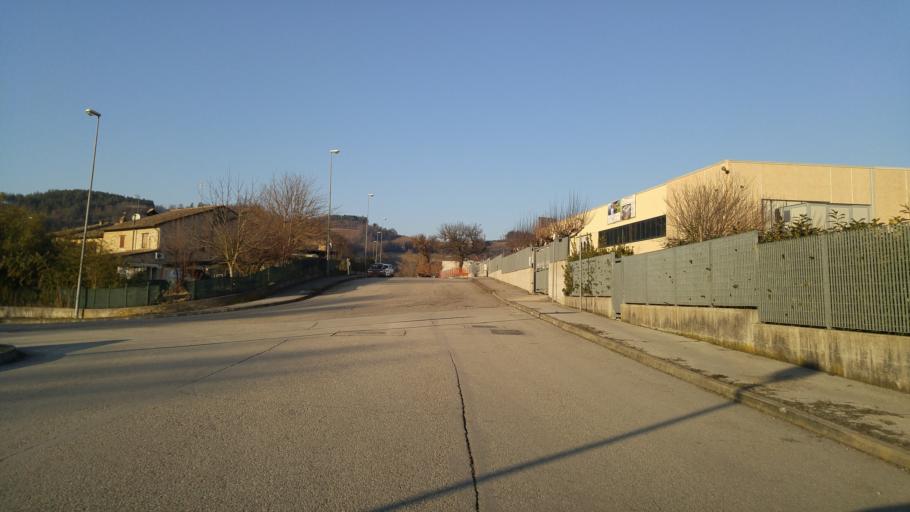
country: IT
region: The Marches
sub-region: Provincia di Pesaro e Urbino
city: Fermignano
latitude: 43.6876
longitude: 12.6465
